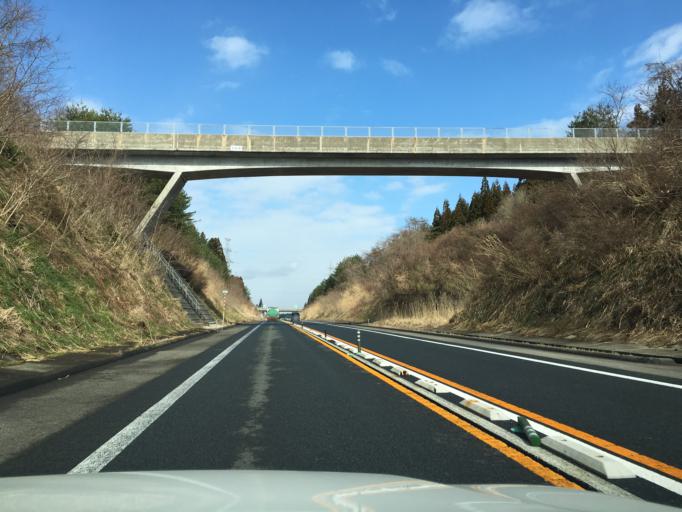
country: JP
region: Akita
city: Akita Shi
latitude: 39.8086
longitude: 140.0940
